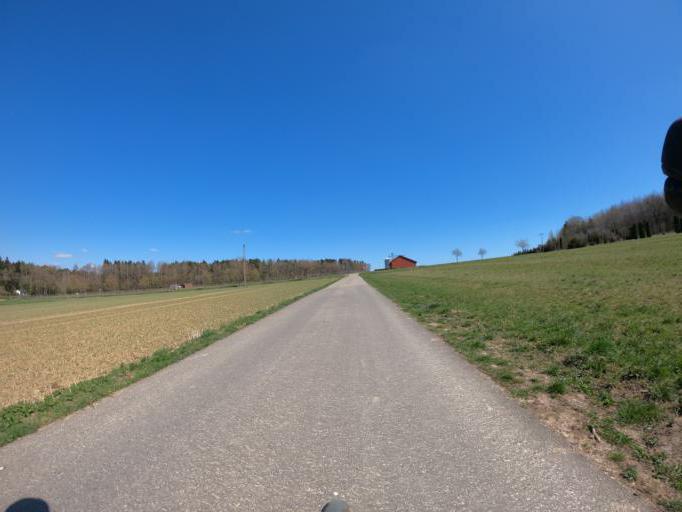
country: DE
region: Baden-Wuerttemberg
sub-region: Karlsruhe Region
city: Empfingen
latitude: 48.4075
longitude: 8.7385
